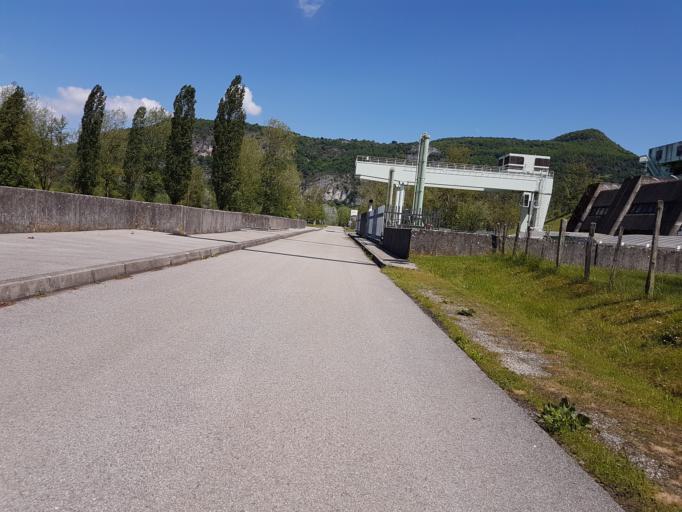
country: FR
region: Rhone-Alpes
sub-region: Departement de l'Isere
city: Les Avenieres
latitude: 45.6540
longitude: 5.6035
